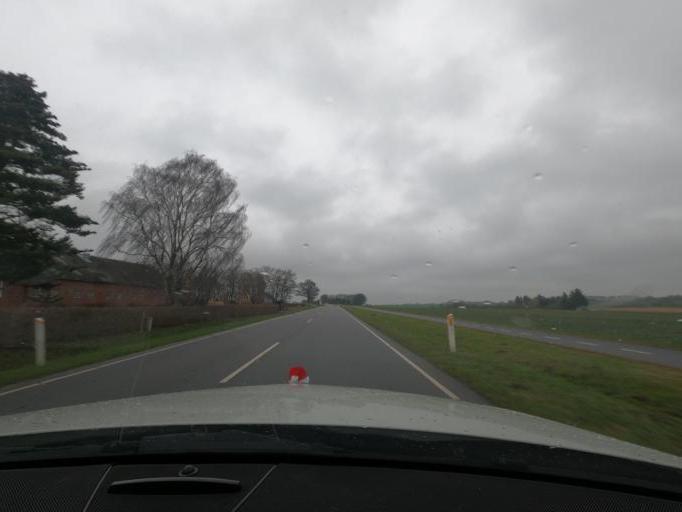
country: DK
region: South Denmark
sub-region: Haderslev Kommune
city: Starup
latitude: 55.2500
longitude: 9.5891
